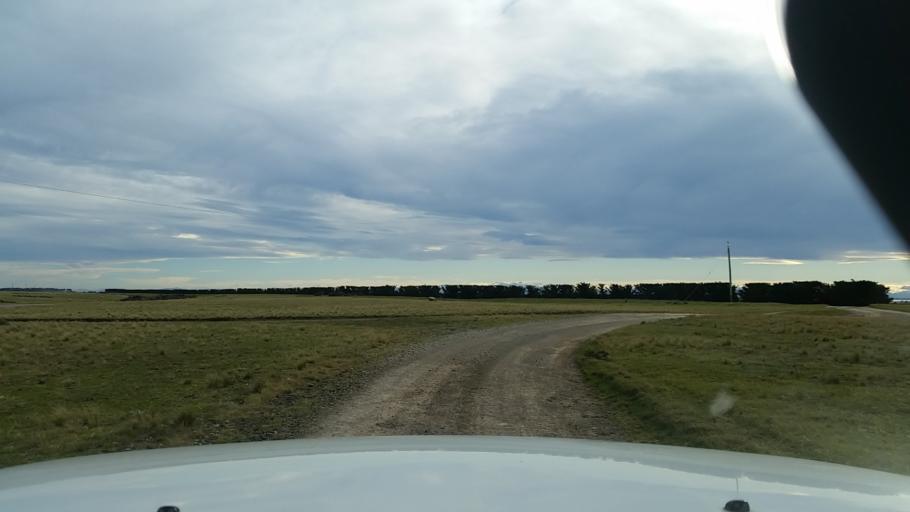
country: NZ
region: Canterbury
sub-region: Selwyn District
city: Lincoln
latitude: -43.8147
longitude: 172.6379
